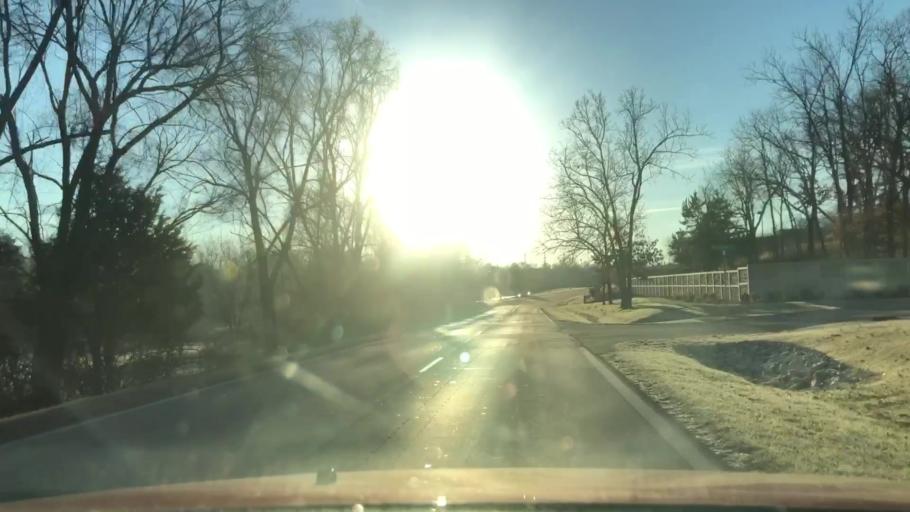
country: US
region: Missouri
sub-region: Greene County
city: Springfield
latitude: 37.1609
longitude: -93.2432
